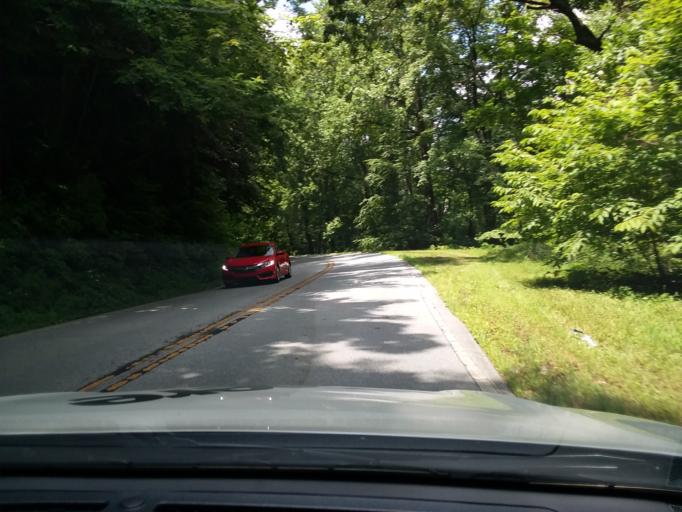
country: US
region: Georgia
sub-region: Rabun County
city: Mountain City
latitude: 35.0144
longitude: -83.1887
